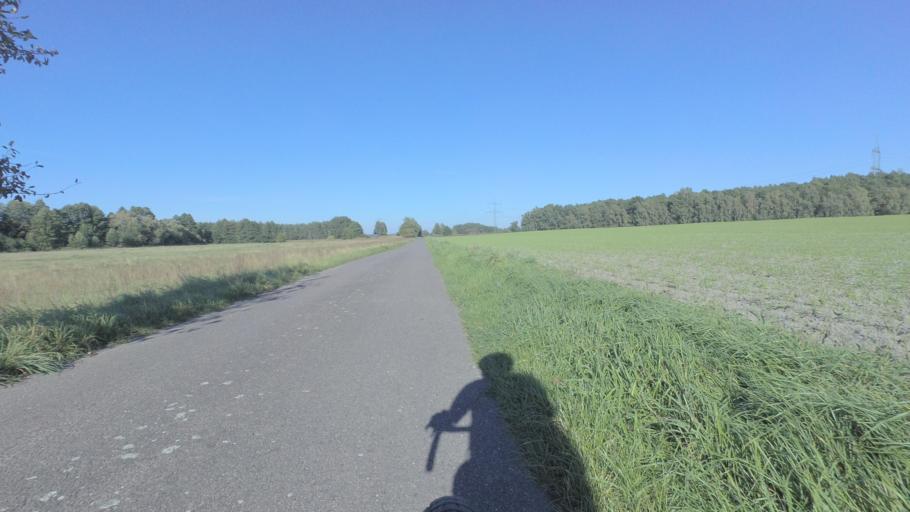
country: DE
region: Brandenburg
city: Sperenberg
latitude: 52.1969
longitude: 13.3355
